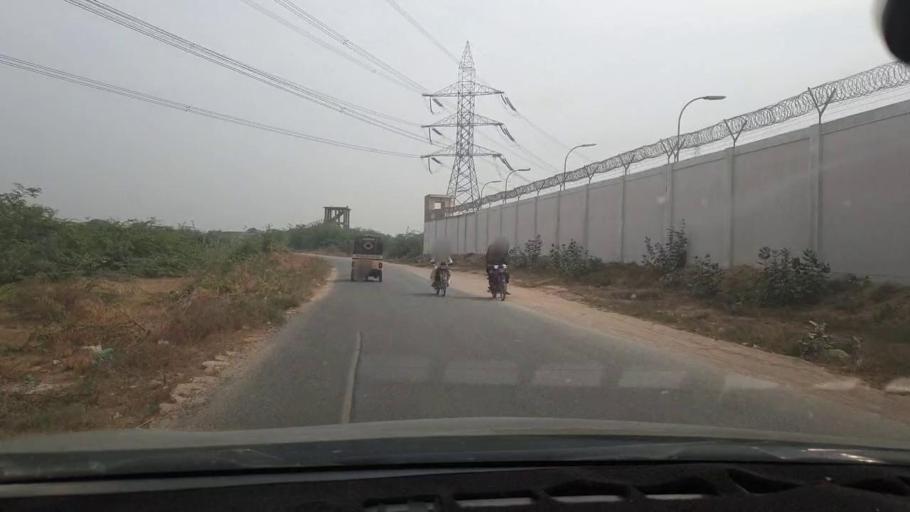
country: PK
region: Sindh
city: Malir Cantonment
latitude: 24.9107
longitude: 67.2840
